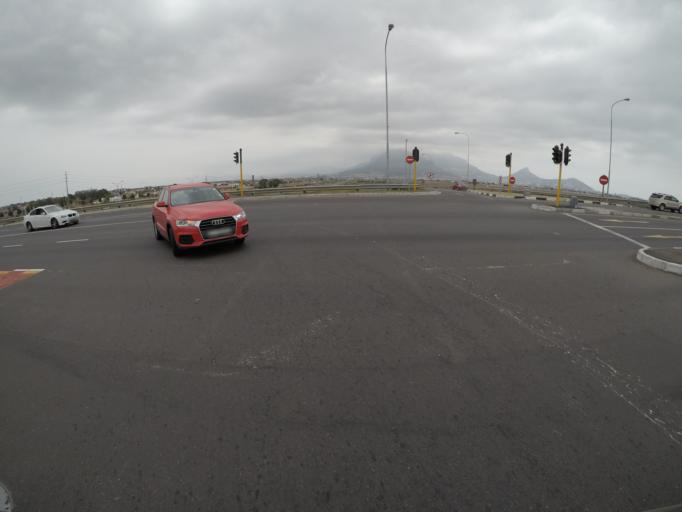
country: ZA
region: Western Cape
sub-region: City of Cape Town
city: Sunset Beach
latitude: -33.9001
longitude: 18.5088
